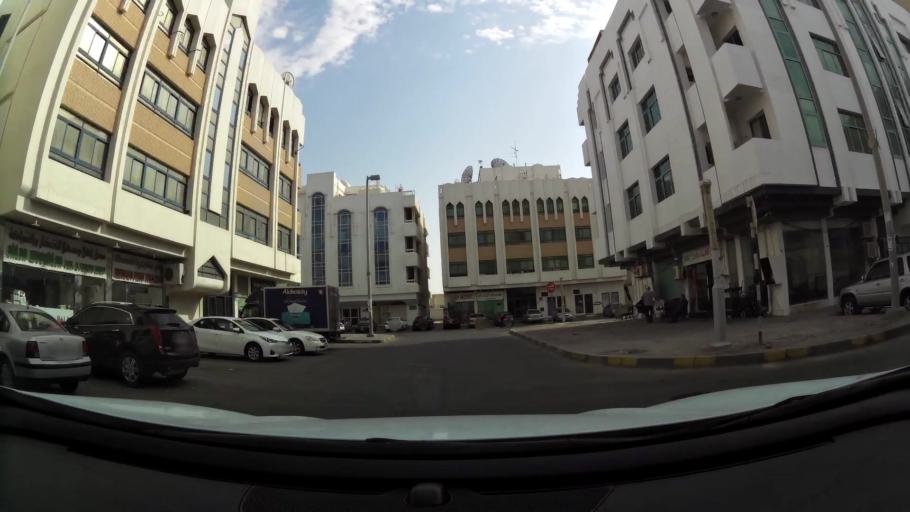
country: AE
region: Abu Dhabi
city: Abu Dhabi
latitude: 24.3225
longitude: 54.5347
